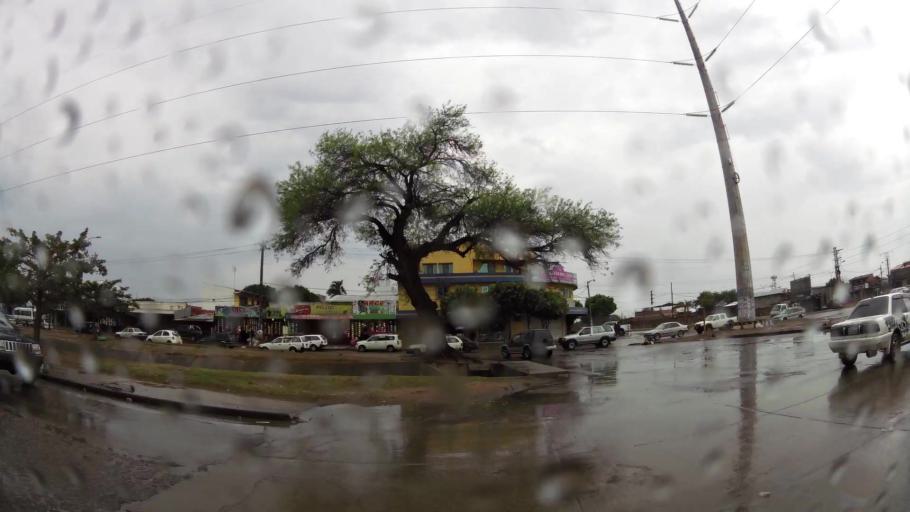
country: BO
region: Santa Cruz
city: Santa Cruz de la Sierra
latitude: -17.7887
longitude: -63.1484
